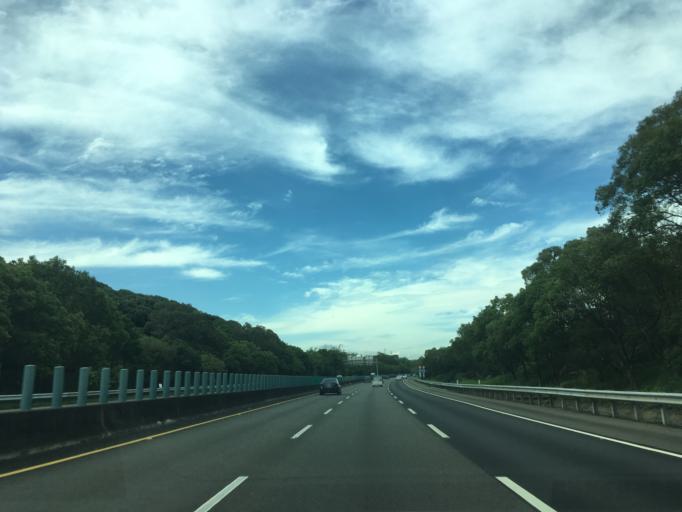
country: TW
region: Taiwan
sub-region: Chiayi
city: Jiayi Shi
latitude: 23.5298
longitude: 120.4876
